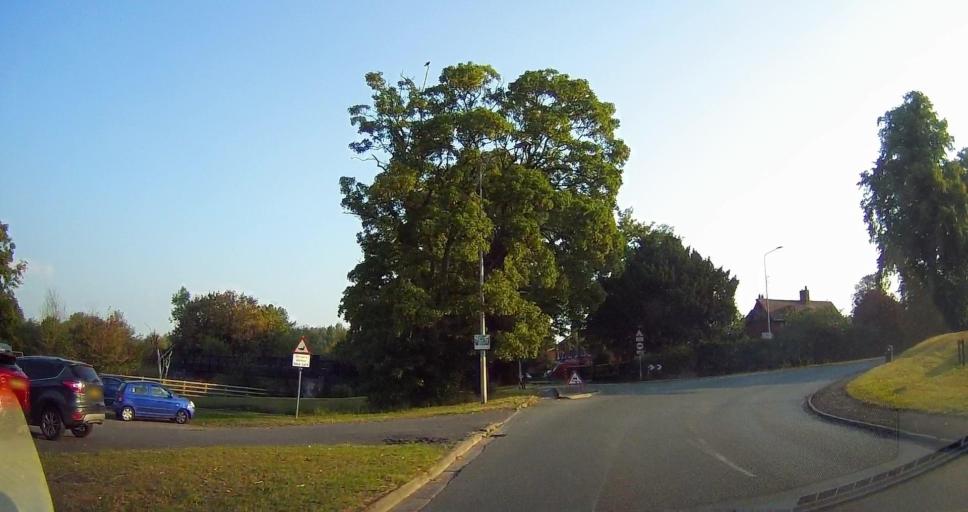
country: GB
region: England
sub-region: Cheshire East
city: Nantwich
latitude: 53.0578
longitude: -2.5237
